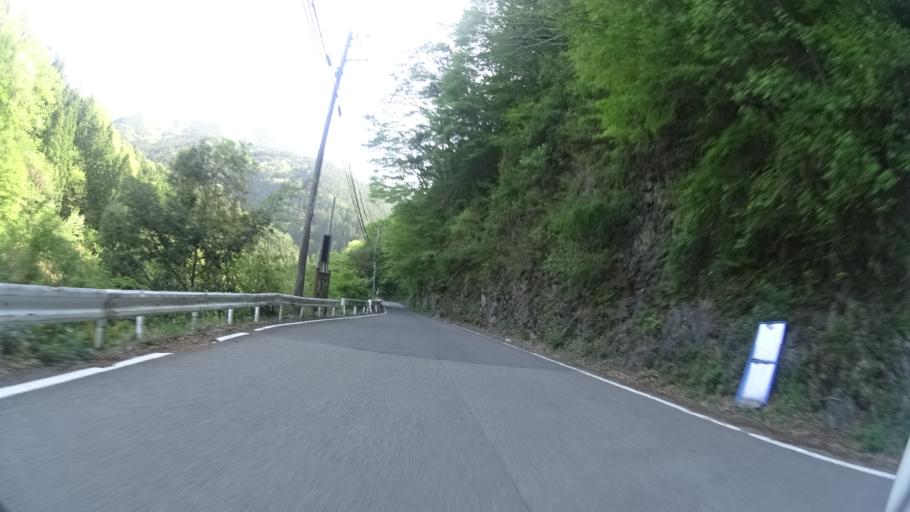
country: JP
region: Tokushima
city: Ikedacho
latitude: 33.8718
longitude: 133.9768
